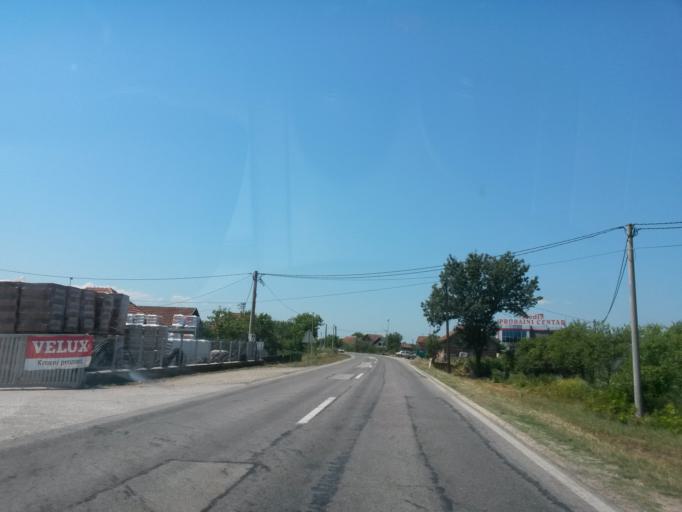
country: BA
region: Republika Srpska
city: Bosanski Samac
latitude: 45.0396
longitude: 18.4472
